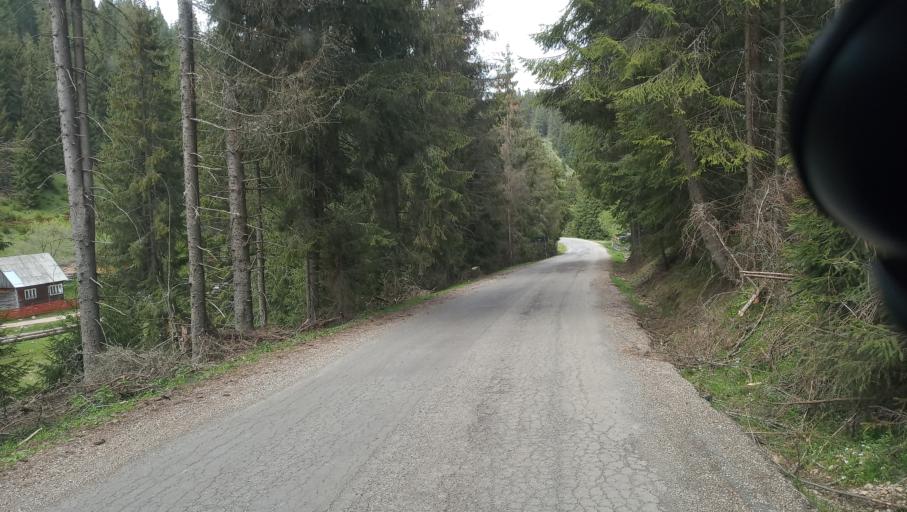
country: RO
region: Alba
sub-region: Comuna Horea
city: Horea
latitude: 46.5536
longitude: 22.8984
